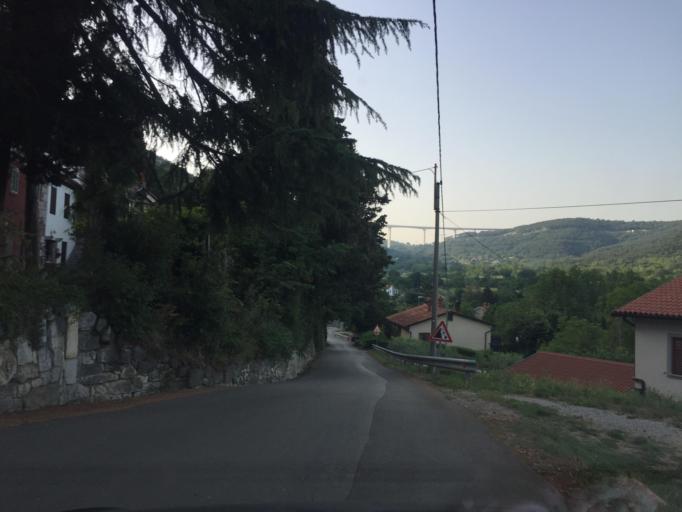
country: IT
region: Friuli Venezia Giulia
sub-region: Provincia di Trieste
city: Dolina
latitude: 45.5728
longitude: 13.8562
